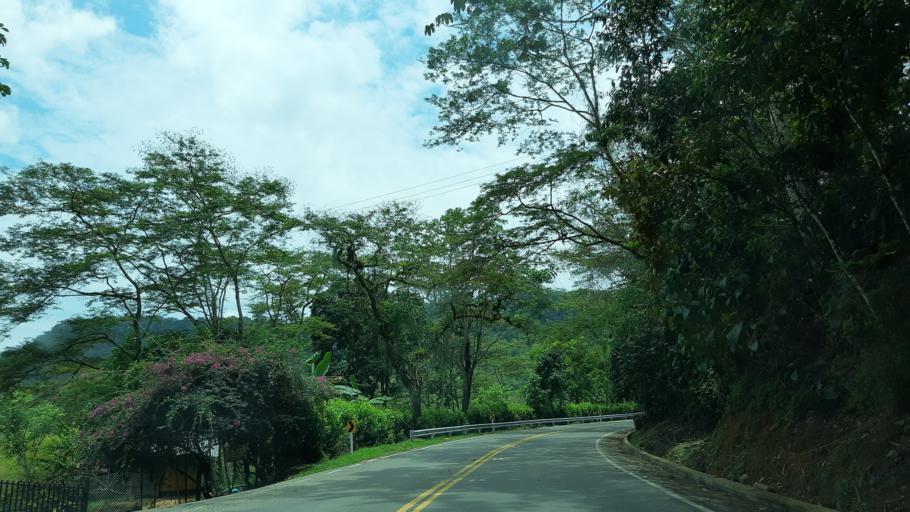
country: CO
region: Casanare
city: Sabanalarga
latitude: 4.8253
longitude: -73.0920
